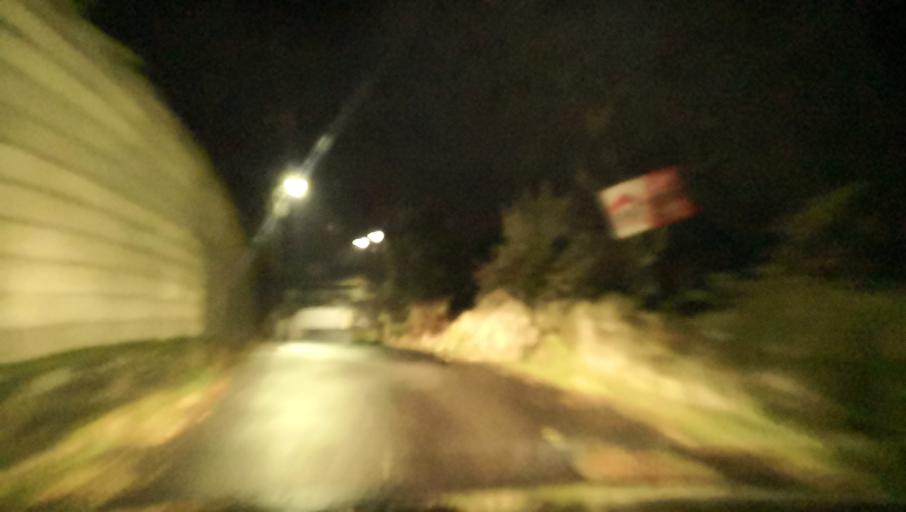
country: PT
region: Vila Real
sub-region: Vila Real
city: Vila Real
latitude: 41.3291
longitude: -7.7278
